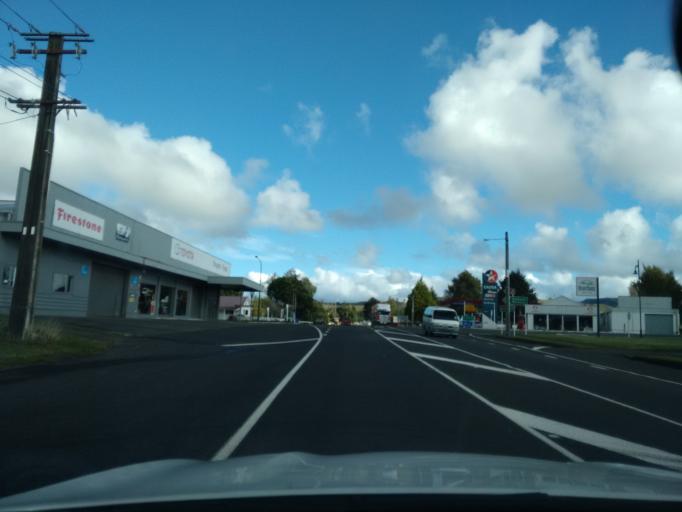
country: NZ
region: Manawatu-Wanganui
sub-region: Ruapehu District
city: Waiouru
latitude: -39.4270
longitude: 175.2819
